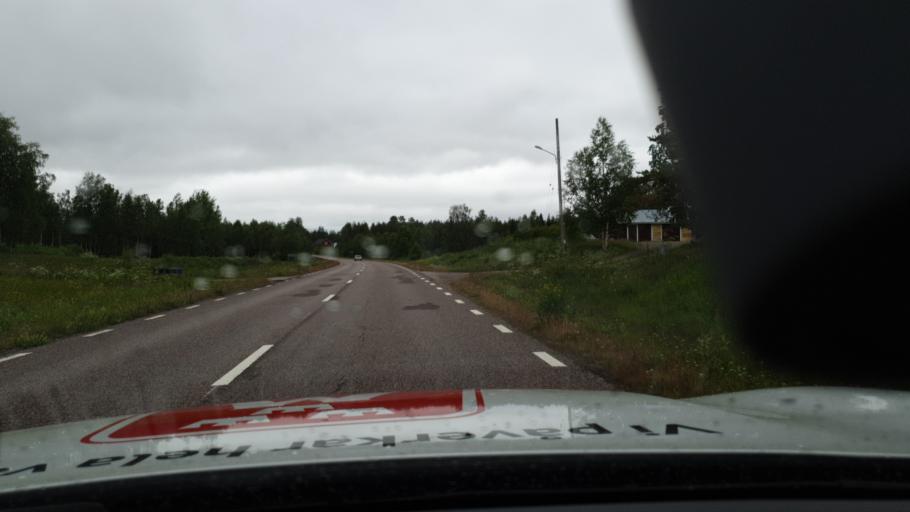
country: FI
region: Lapland
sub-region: Torniolaakso
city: Pello
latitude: 66.9657
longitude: 23.8198
